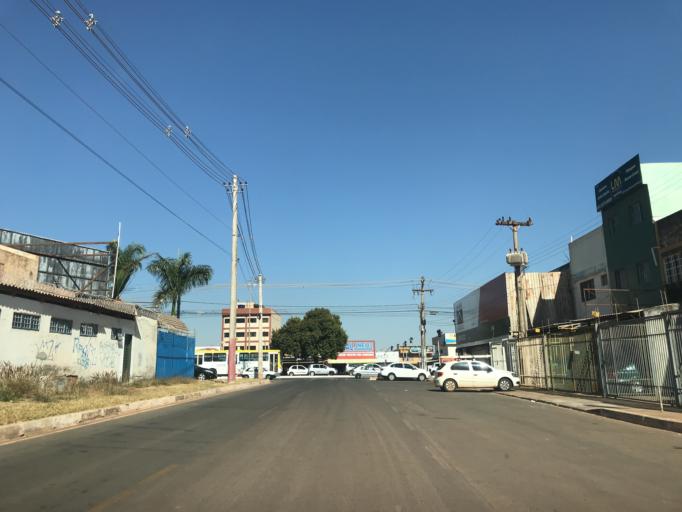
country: BR
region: Federal District
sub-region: Brasilia
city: Brasilia
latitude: -15.8503
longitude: -48.0404
